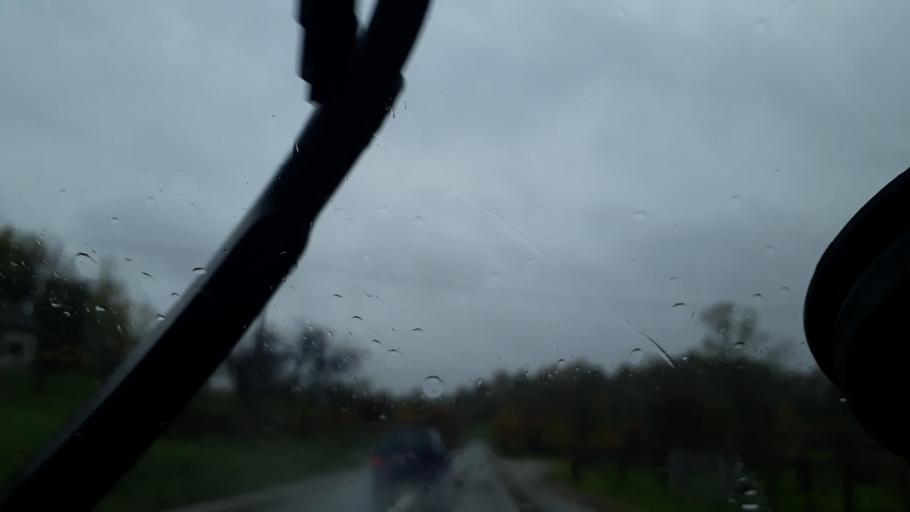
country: BA
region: Republika Srpska
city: Maglajani
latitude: 44.8681
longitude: 17.4686
